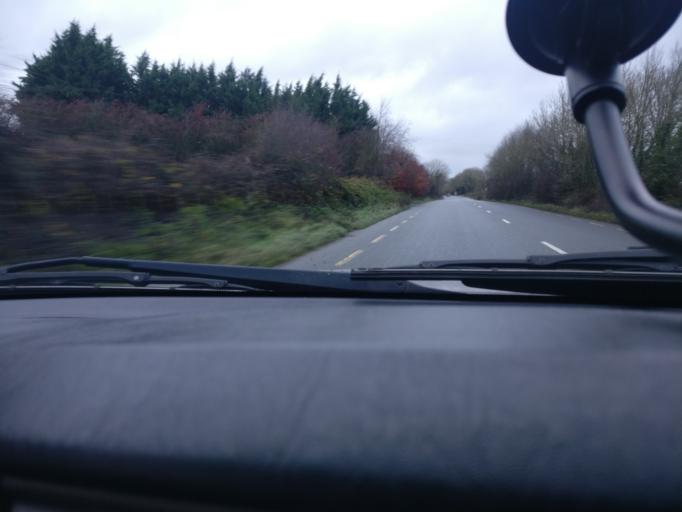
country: IE
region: Leinster
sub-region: Kildare
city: Kilcock
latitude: 53.4158
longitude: -6.7230
